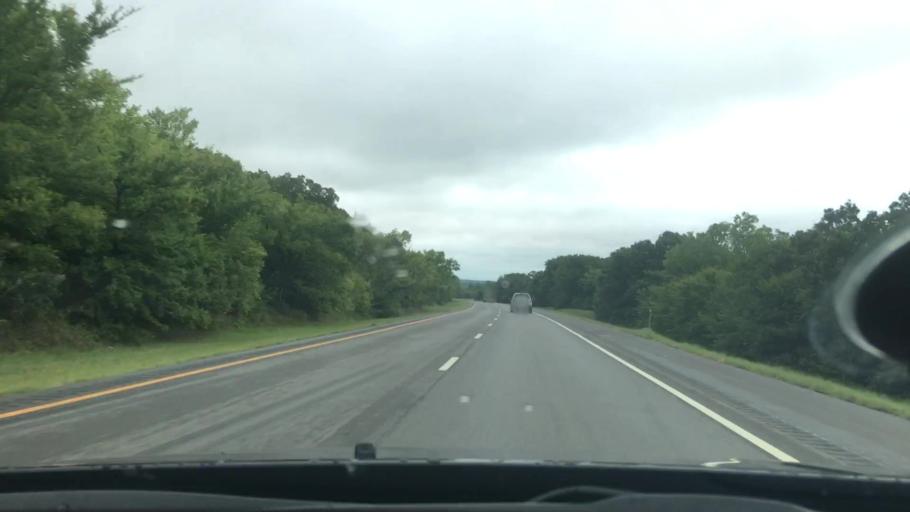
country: US
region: Oklahoma
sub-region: Okmulgee County
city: Morris
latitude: 35.4427
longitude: -95.7758
